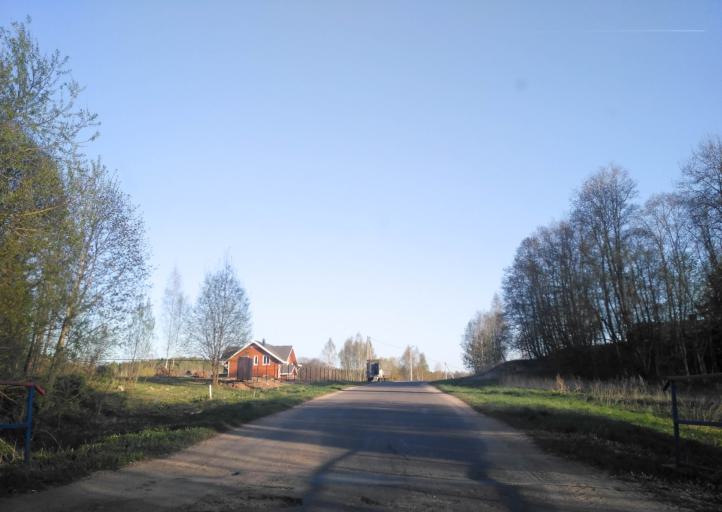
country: BY
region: Minsk
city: Pyatryshki
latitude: 54.1099
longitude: 27.1908
